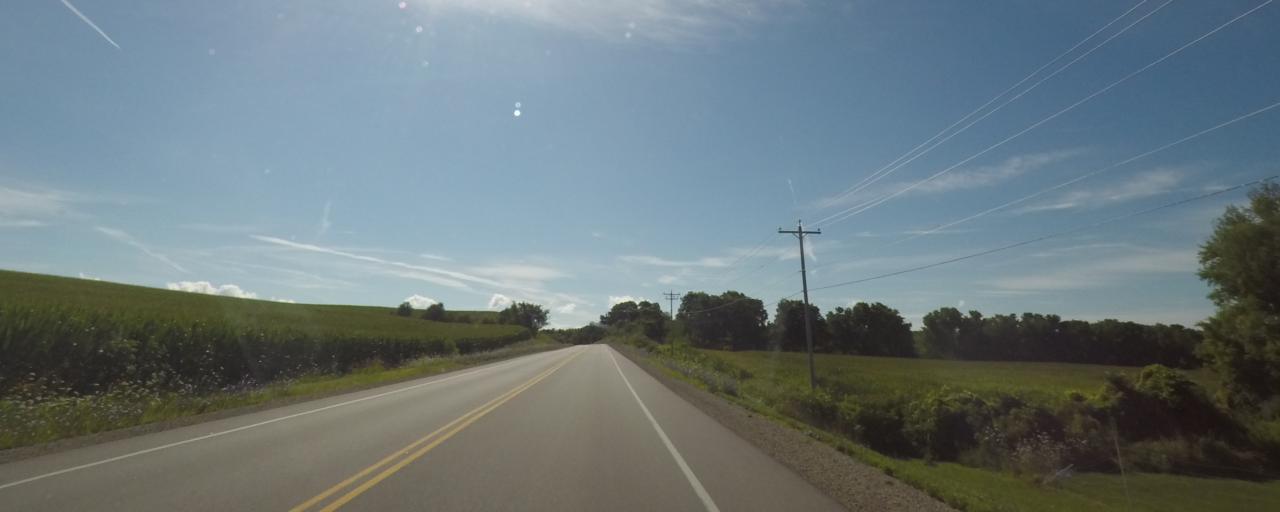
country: US
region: Wisconsin
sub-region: Jefferson County
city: Johnson Creek
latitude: 43.0748
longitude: -88.7123
